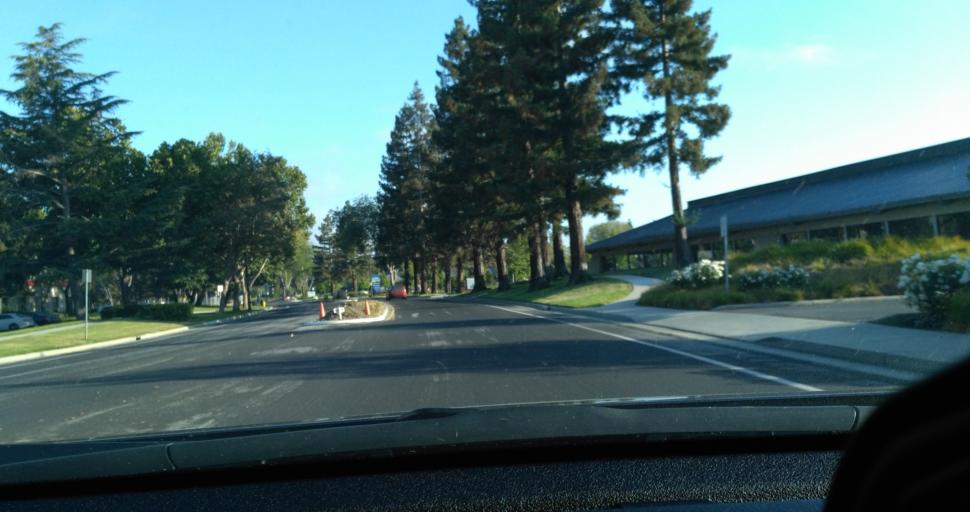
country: US
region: California
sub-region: Santa Clara County
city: Santa Clara
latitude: 37.3872
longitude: -121.9333
